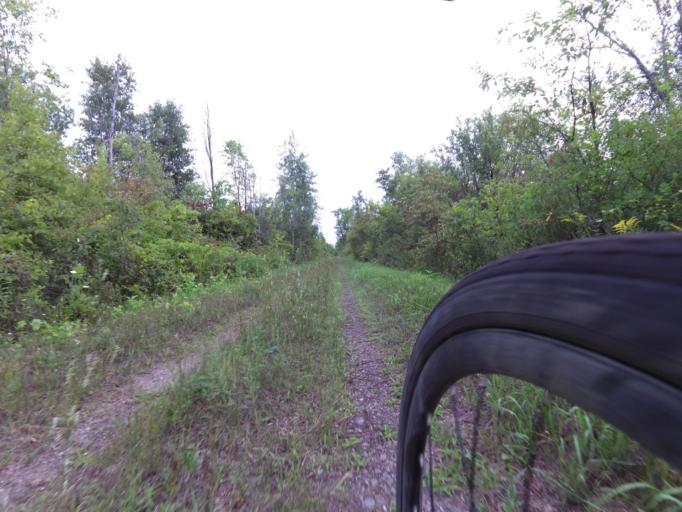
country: CA
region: Ontario
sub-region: Lanark County
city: Smiths Falls
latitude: 44.7604
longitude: -76.1195
